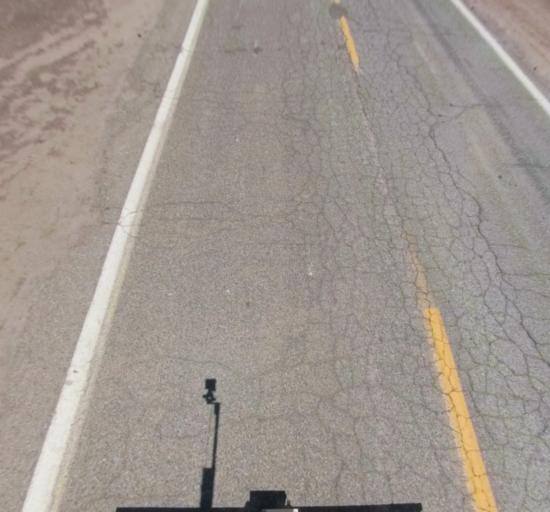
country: US
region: California
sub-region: Madera County
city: Chowchilla
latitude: 37.0400
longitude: -120.2820
